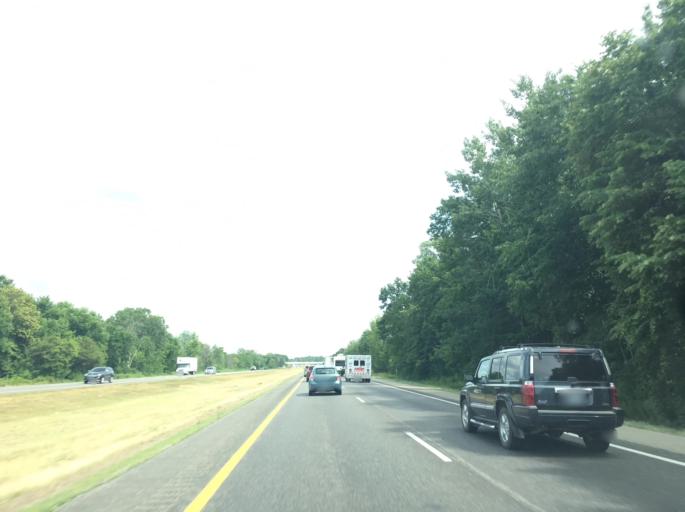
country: US
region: Michigan
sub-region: Genesee County
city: Grand Blanc
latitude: 42.9348
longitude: -83.7005
